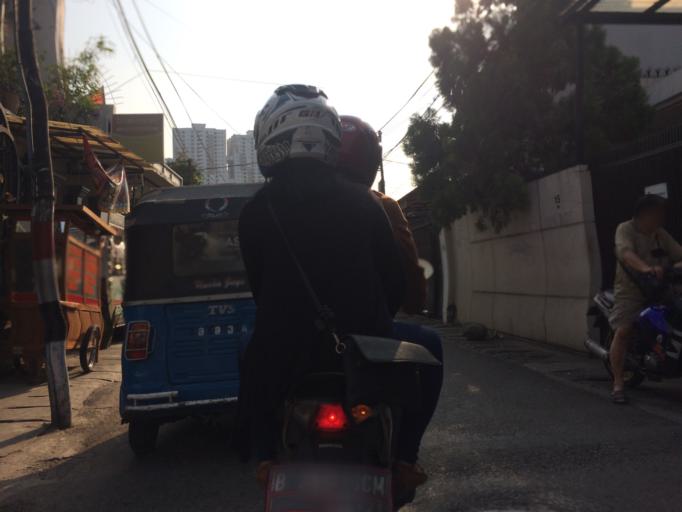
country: ID
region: Jakarta Raya
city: Jakarta
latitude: -6.2142
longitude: 106.8417
